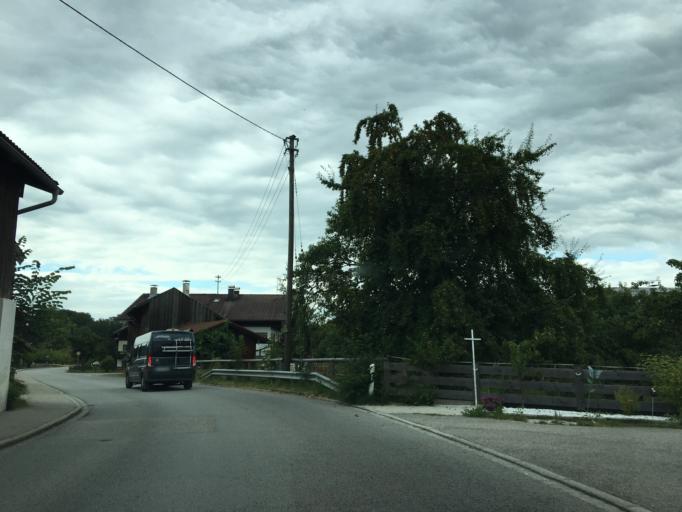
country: DE
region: Bavaria
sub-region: Upper Bavaria
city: Bad Feilnbach
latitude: 47.7756
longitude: 12.0127
